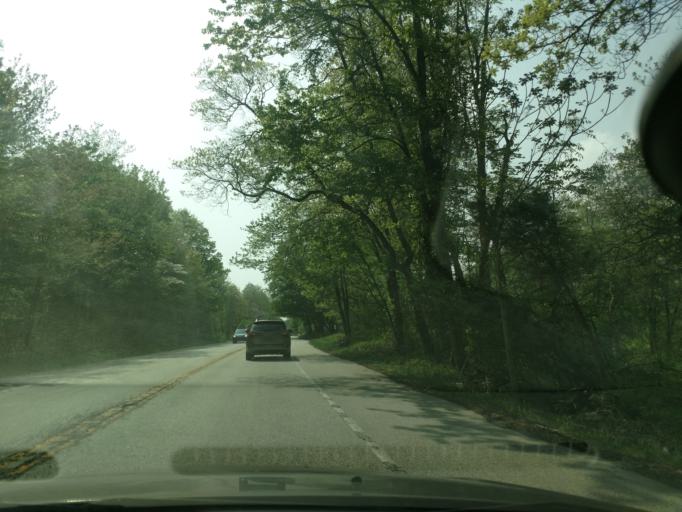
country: US
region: Pennsylvania
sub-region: Chester County
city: Elverson
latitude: 40.1631
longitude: -75.7724
